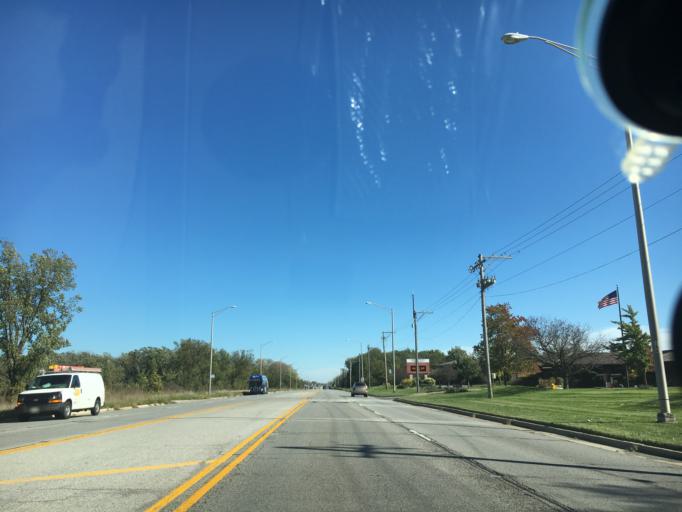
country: US
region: Illinois
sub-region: Cook County
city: Tinley Park
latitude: 41.6024
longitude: -87.7830
